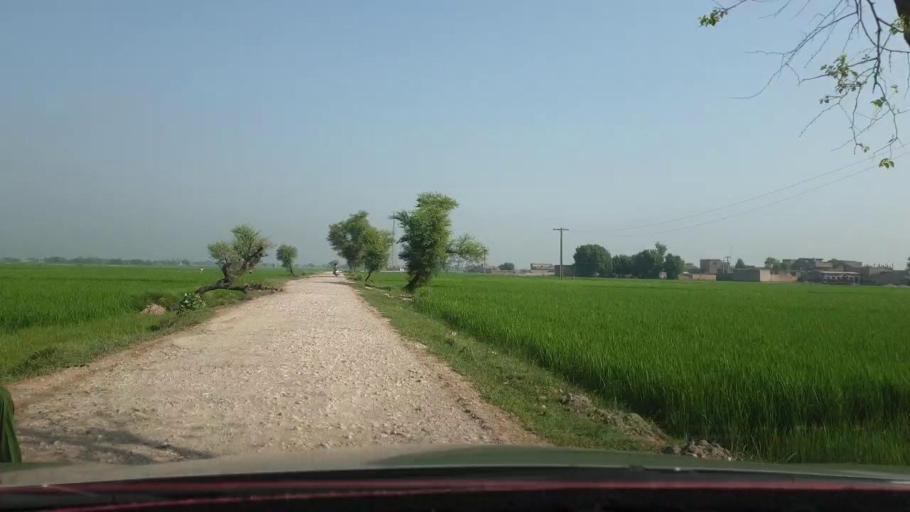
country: PK
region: Sindh
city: Nasirabad
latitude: 27.4817
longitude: 67.9256
